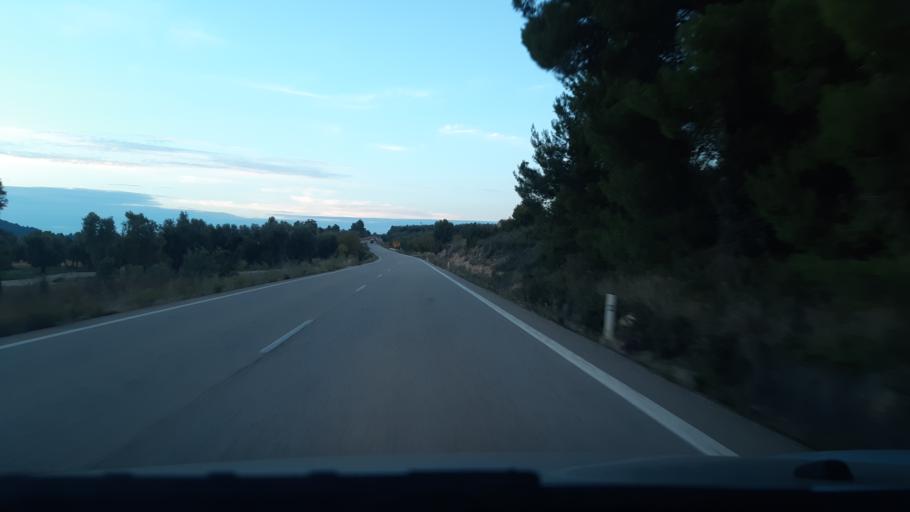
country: ES
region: Aragon
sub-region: Provincia de Teruel
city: Valderrobres
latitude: 40.8560
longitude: 0.1717
